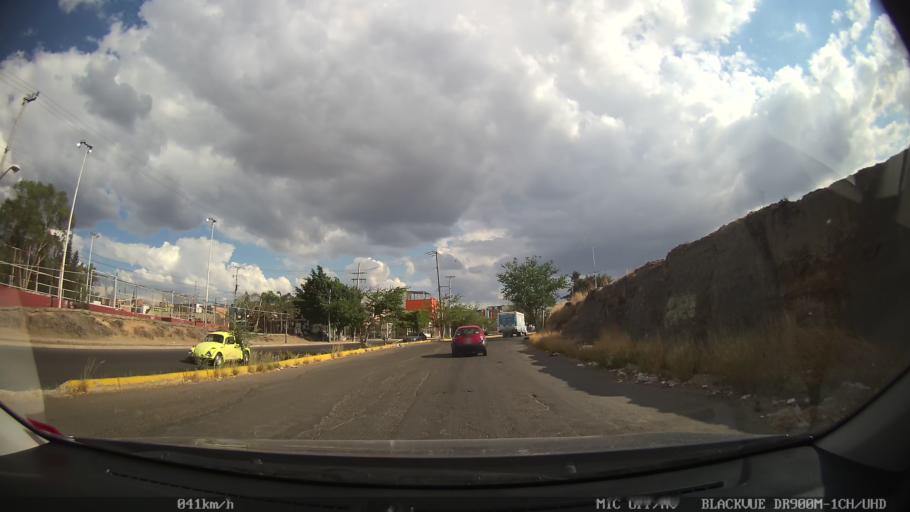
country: MX
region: Jalisco
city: Tlaquepaque
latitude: 20.6401
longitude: -103.2808
